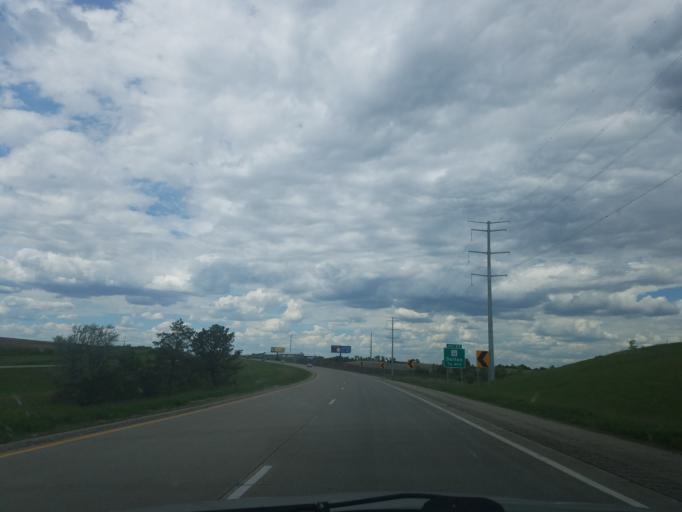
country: US
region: Minnesota
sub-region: Grant County
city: Elbow Lake
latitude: 46.1389
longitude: -95.9255
